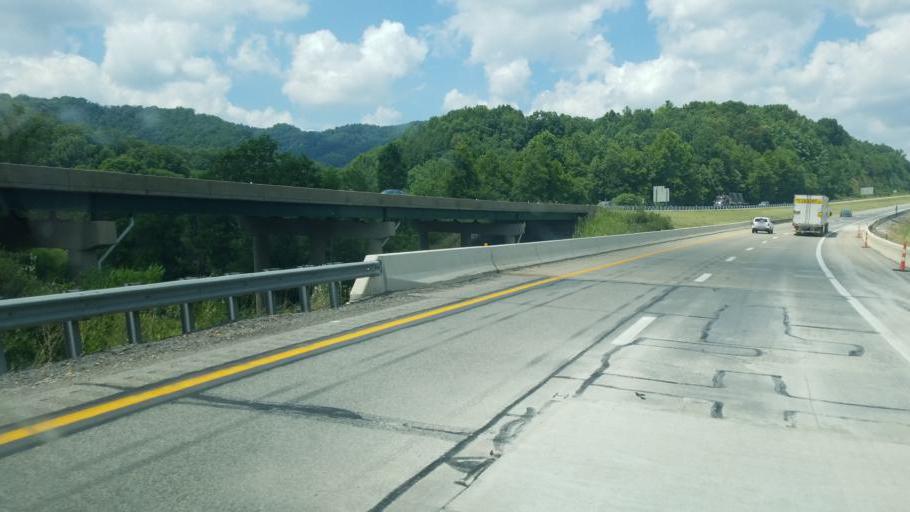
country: US
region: West Virginia
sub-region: Raleigh County
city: Bradley
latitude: 37.8792
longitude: -81.2667
